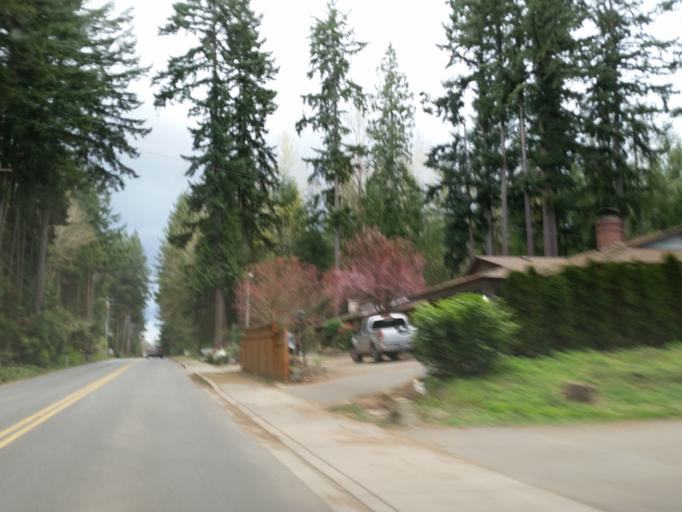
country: US
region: Washington
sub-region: King County
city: Woodinville
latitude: 47.7829
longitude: -122.1725
